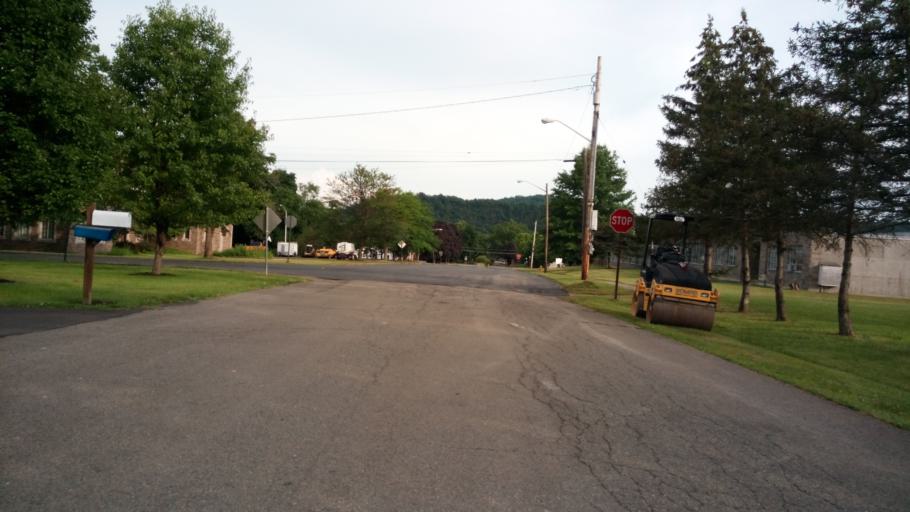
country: US
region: New York
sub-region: Chemung County
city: West Elmira
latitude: 42.0836
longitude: -76.8374
